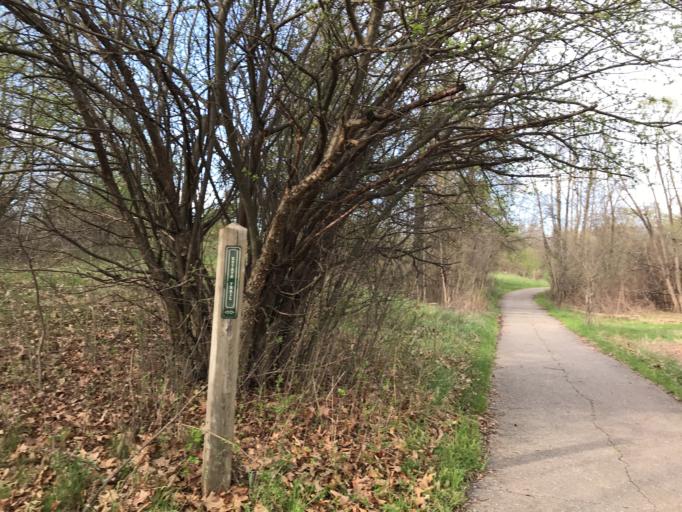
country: US
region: Michigan
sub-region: Oakland County
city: Farmington Hills
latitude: 42.4753
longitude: -83.3818
